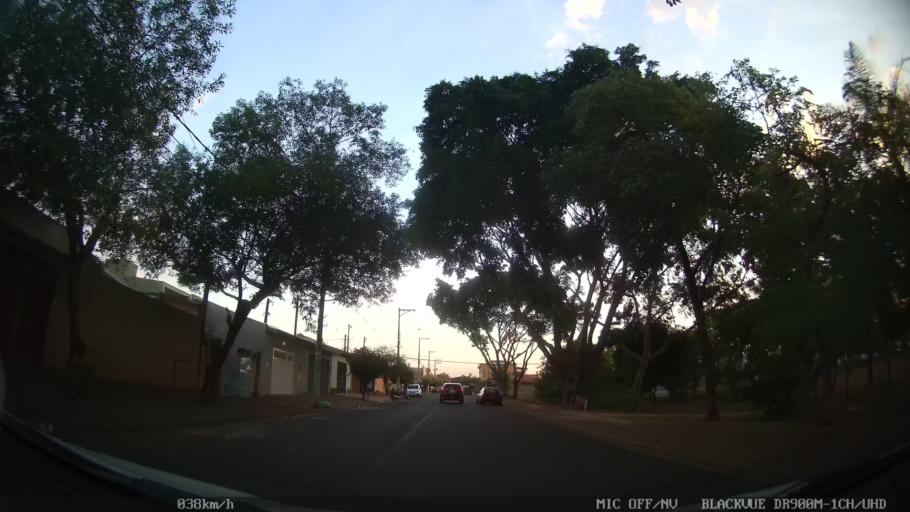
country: BR
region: Sao Paulo
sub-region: Ribeirao Preto
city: Ribeirao Preto
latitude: -21.1400
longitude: -47.8223
